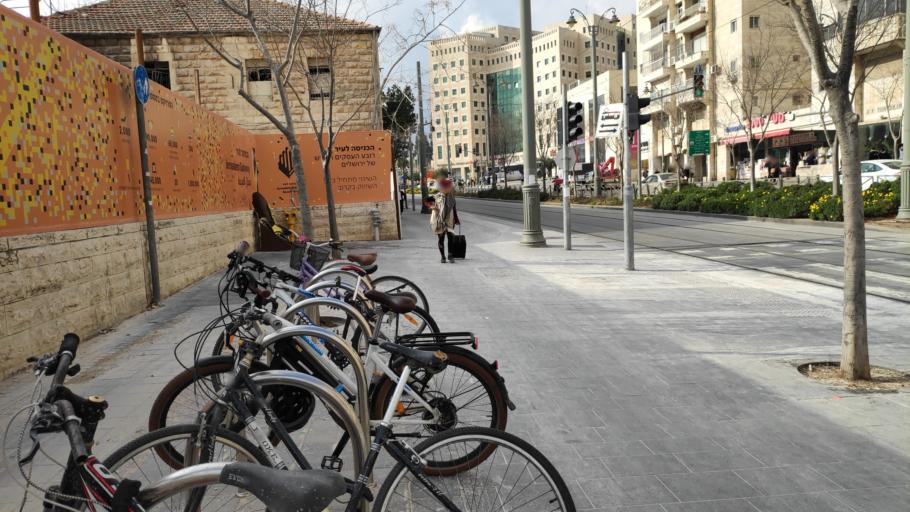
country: IL
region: Jerusalem
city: West Jerusalem
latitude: 31.7880
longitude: 35.2066
